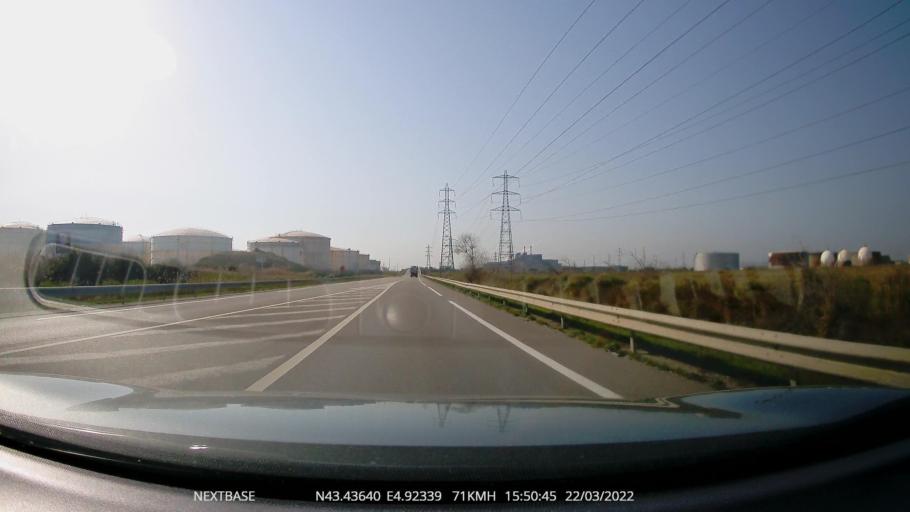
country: FR
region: Provence-Alpes-Cote d'Azur
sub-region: Departement des Bouches-du-Rhone
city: Fos-sur-Mer
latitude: 43.4362
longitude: 4.9245
